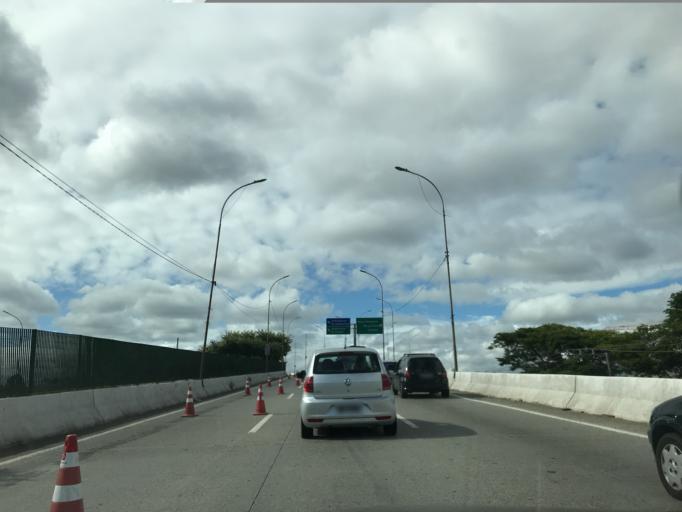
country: BR
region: Sao Paulo
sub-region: Osasco
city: Osasco
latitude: -23.5242
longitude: -46.7733
